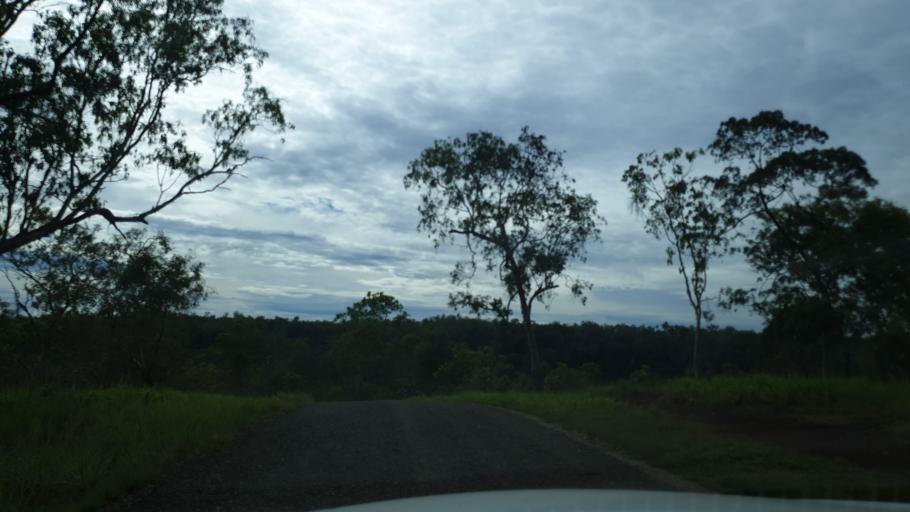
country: PG
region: National Capital
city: Port Moresby
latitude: -9.4326
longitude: 147.3947
